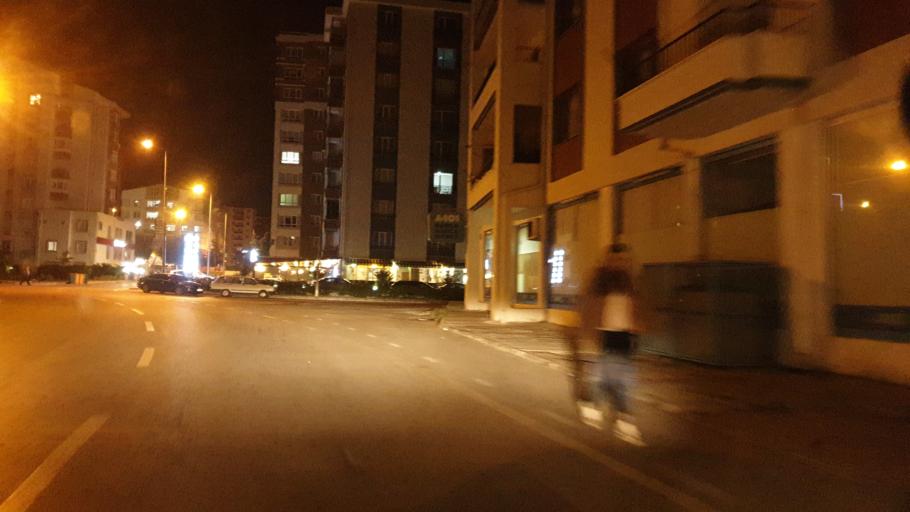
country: TR
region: Kayseri
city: Talas
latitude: 38.6961
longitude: 35.5435
